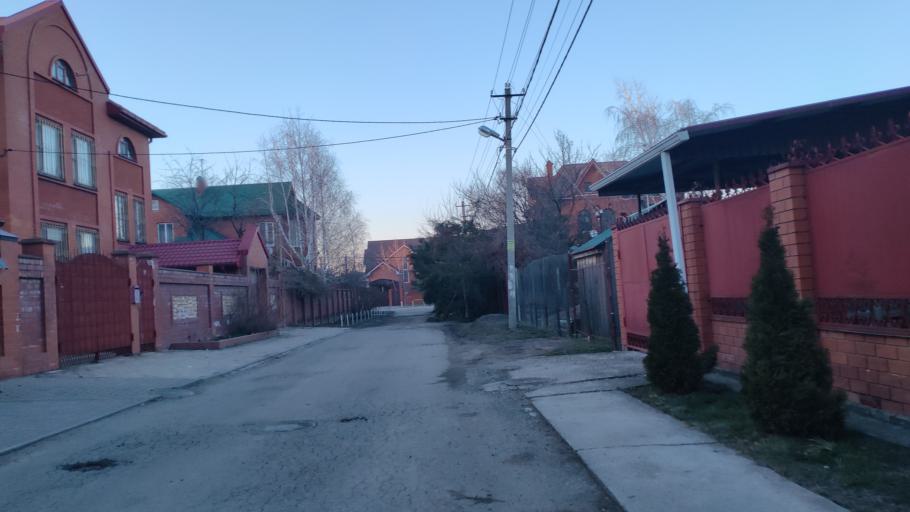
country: RU
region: Krasnodarskiy
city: Krasnodar
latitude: 45.0740
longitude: 39.0062
